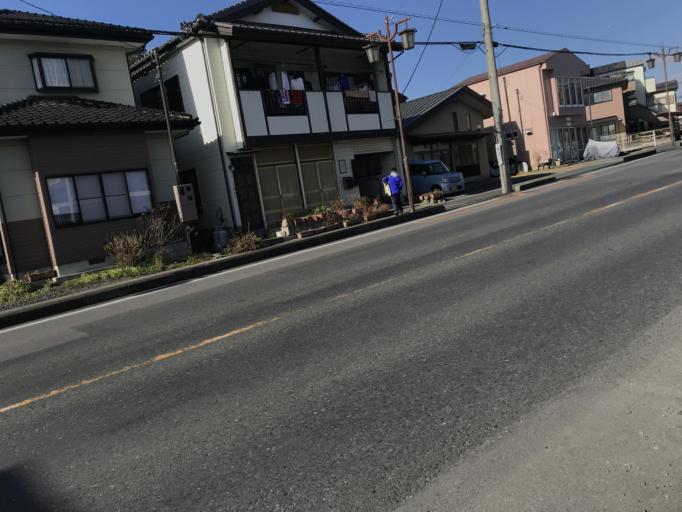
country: JP
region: Tochigi
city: Kanuma
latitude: 36.5763
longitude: 139.7515
